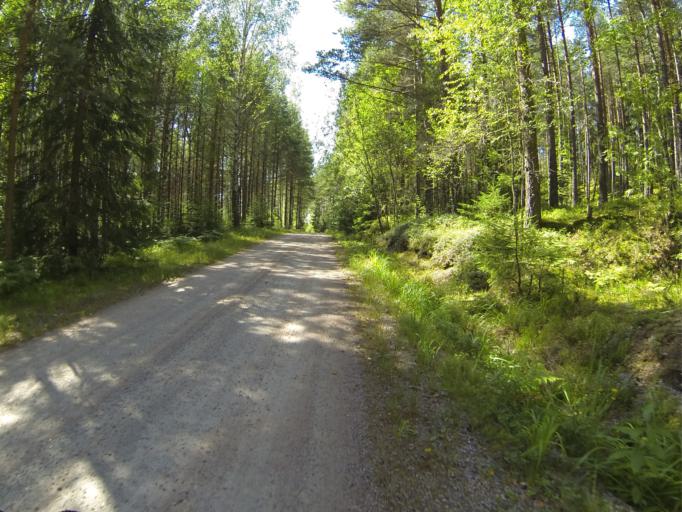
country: FI
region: Varsinais-Suomi
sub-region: Salo
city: Pernioe
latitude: 60.2873
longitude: 23.0769
